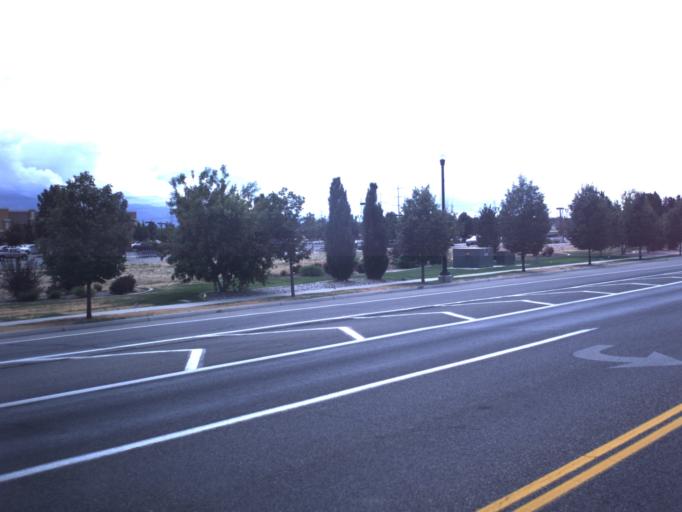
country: US
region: Utah
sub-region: Davis County
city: Clinton
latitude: 41.1542
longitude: -112.0645
